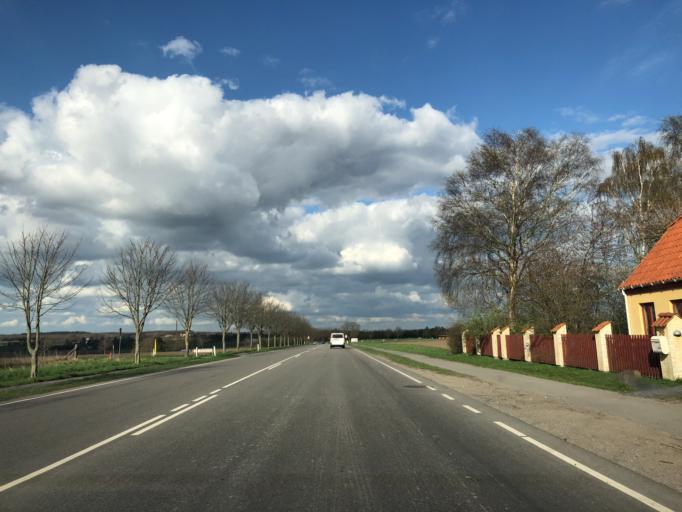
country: DK
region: Zealand
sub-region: Ringsted Kommune
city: Ringsted
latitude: 55.4714
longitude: 11.8224
